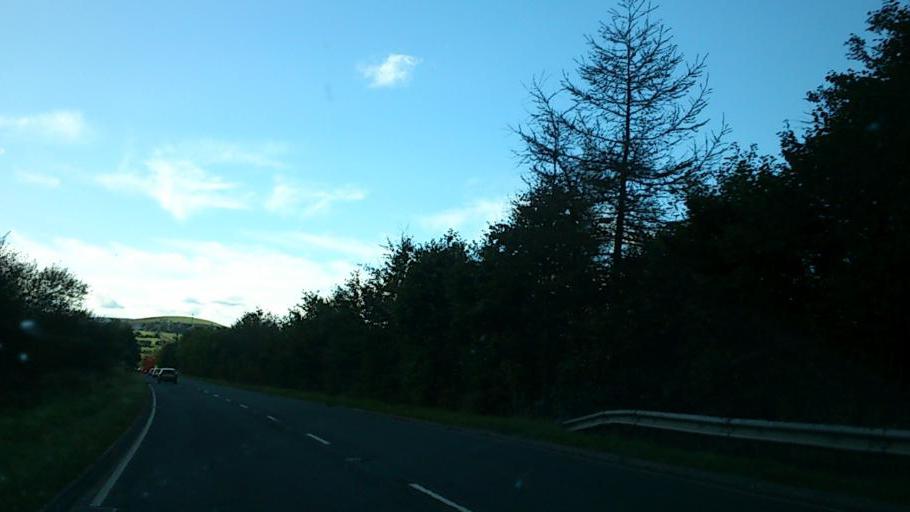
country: GB
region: Wales
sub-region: Sir Powys
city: Llanidloes
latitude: 52.4066
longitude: -3.5904
